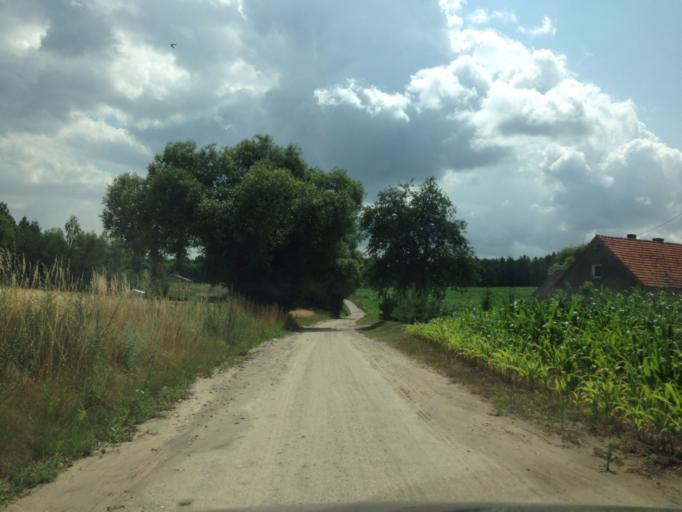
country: PL
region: Kujawsko-Pomorskie
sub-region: Powiat brodnicki
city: Gorzno
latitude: 53.2260
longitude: 19.6461
